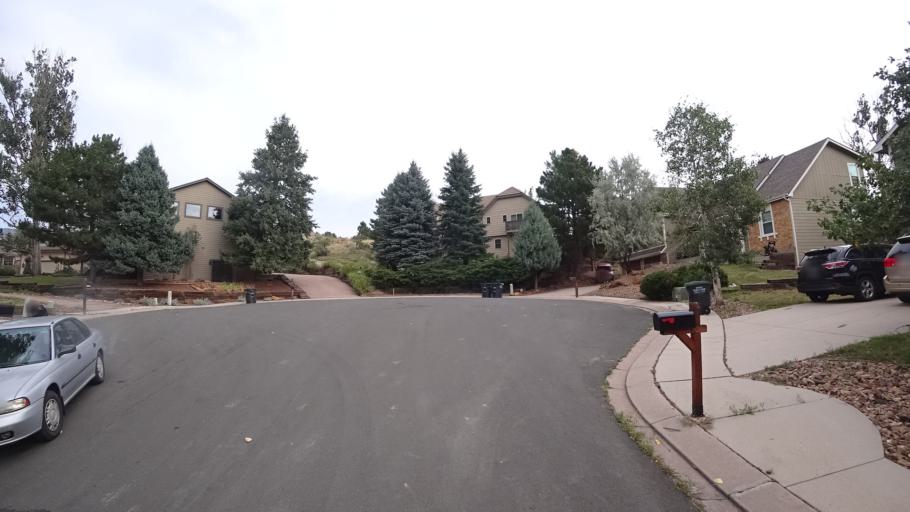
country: US
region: Colorado
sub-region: El Paso County
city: Air Force Academy
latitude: 38.9258
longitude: -104.8451
